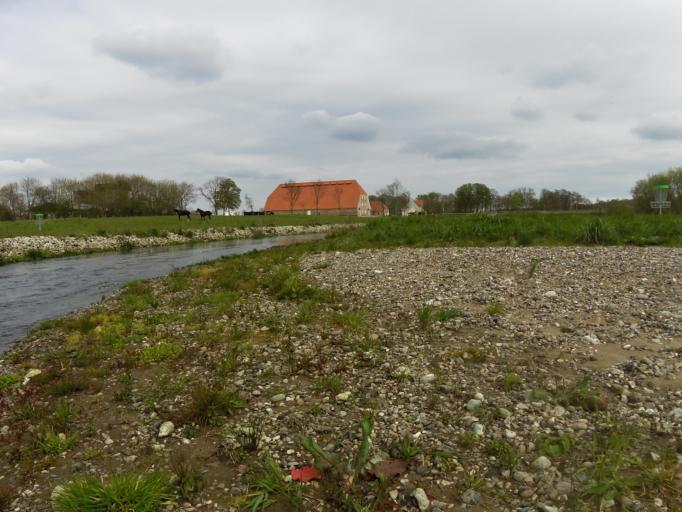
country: DK
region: South Denmark
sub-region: Haderslev Kommune
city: Gram
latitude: 55.2969
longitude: 9.0551
